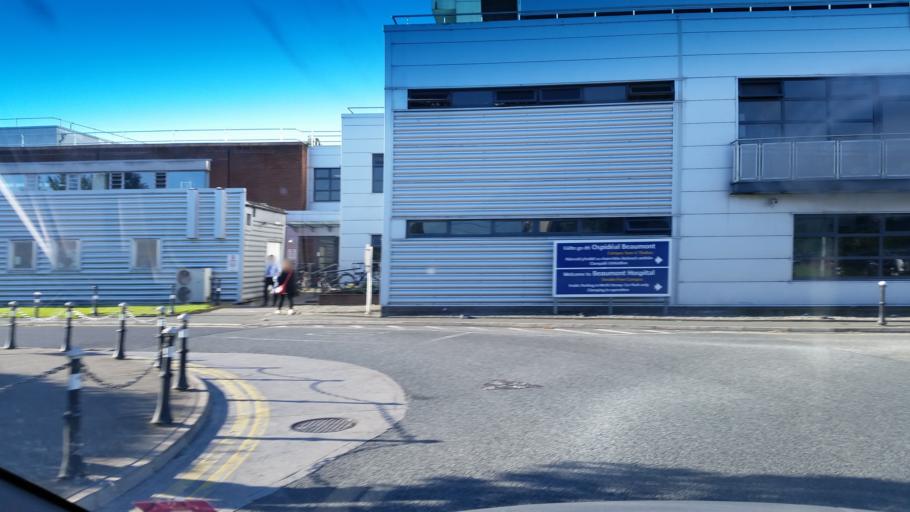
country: IE
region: Leinster
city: Artane
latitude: 53.3922
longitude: -6.2223
